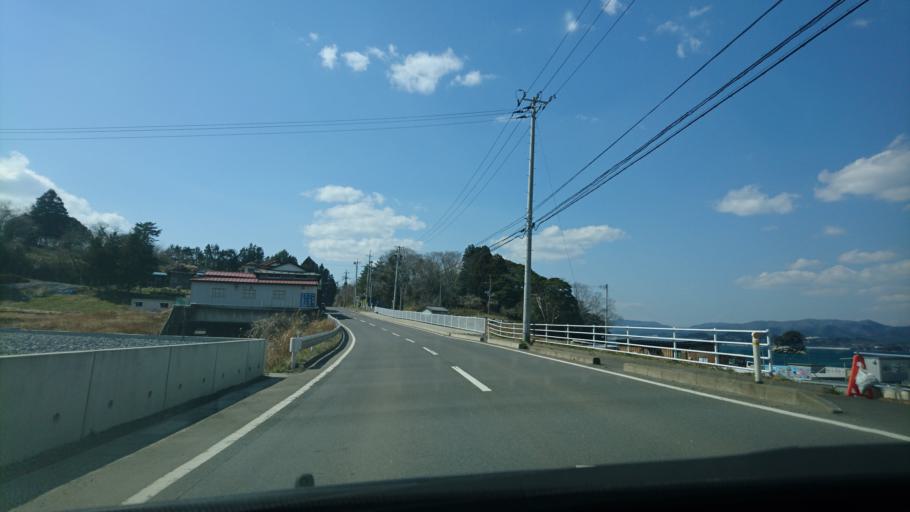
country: JP
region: Miyagi
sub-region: Oshika Gun
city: Onagawa Cho
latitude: 38.6405
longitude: 141.4846
